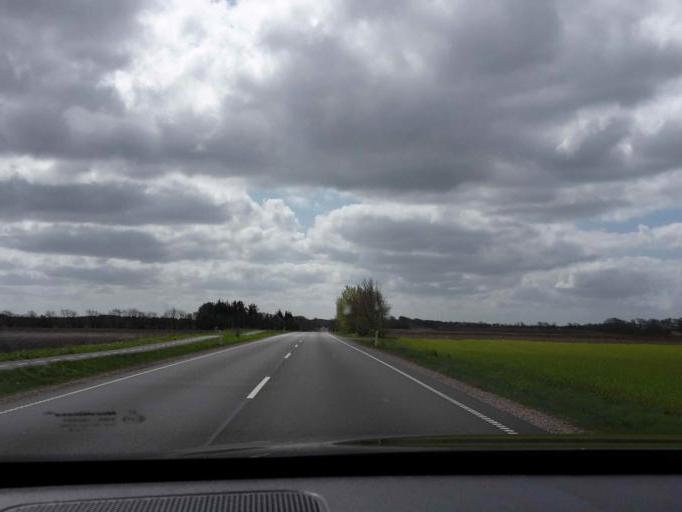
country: DK
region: South Denmark
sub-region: Varde Kommune
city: Olgod
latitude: 55.7431
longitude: 8.6186
